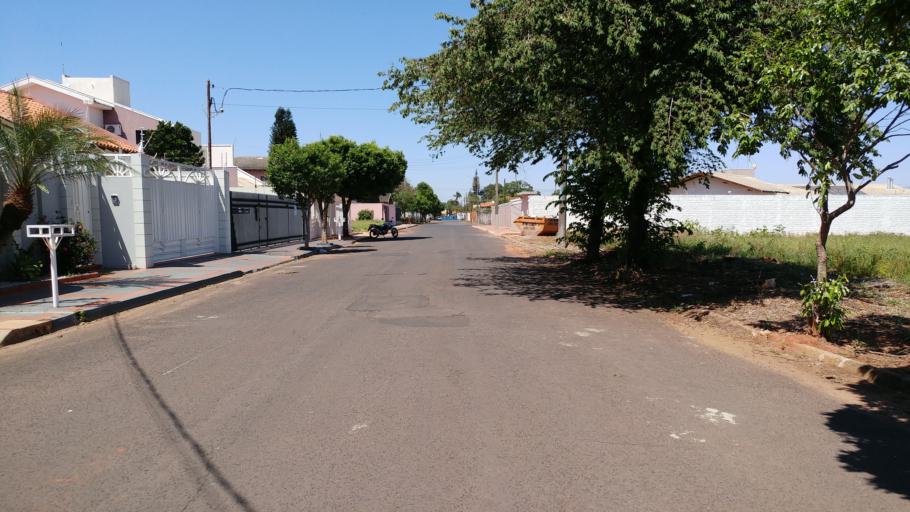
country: BR
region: Sao Paulo
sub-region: Paraguacu Paulista
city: Paraguacu Paulista
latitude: -22.4094
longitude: -50.5833
